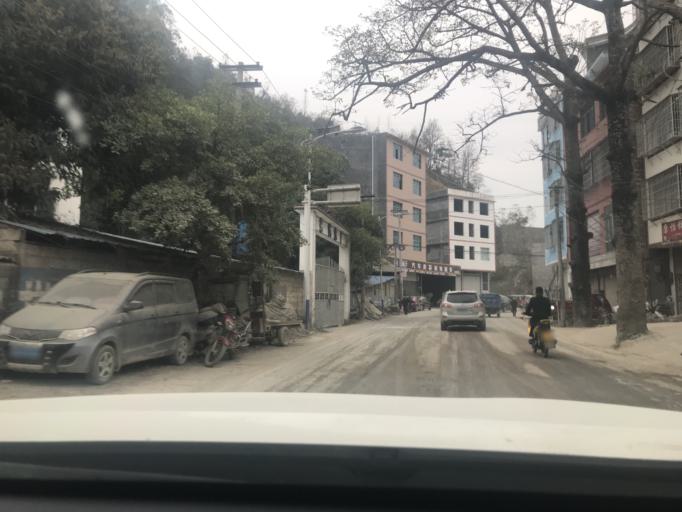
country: CN
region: Guangxi Zhuangzu Zizhiqu
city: Xinzhou
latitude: 24.9814
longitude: 105.8185
